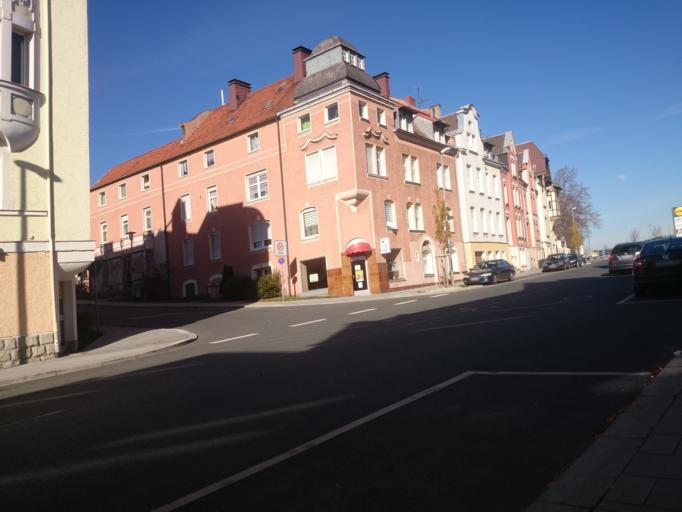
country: DE
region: Bavaria
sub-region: Upper Franconia
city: Hof
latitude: 50.3240
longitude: 11.8986
